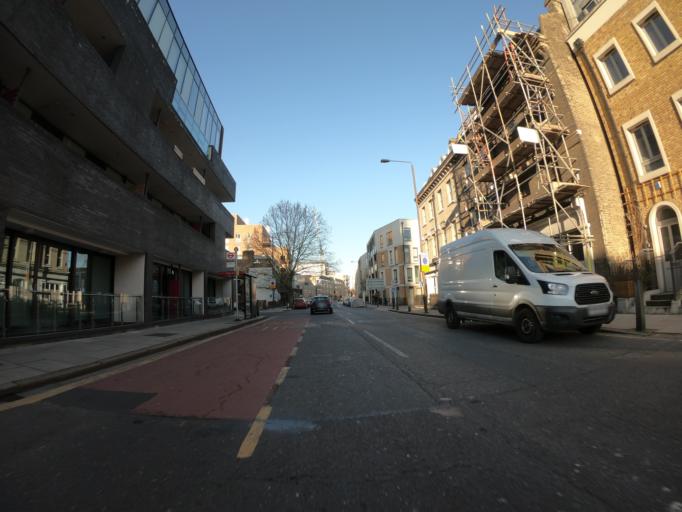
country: GB
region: England
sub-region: Greater London
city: Catford
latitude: 51.4749
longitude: -0.0204
